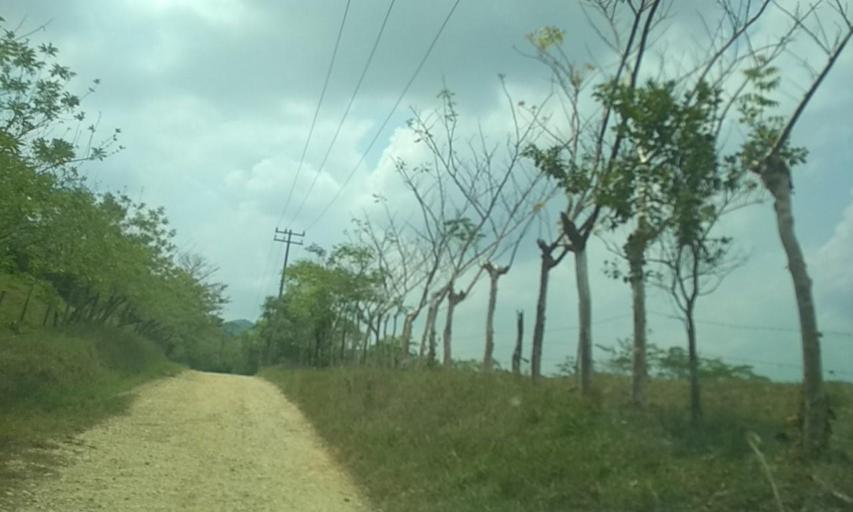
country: MX
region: Tabasco
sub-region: Huimanguillo
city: Francisco Rueda
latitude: 17.5839
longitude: -93.7904
